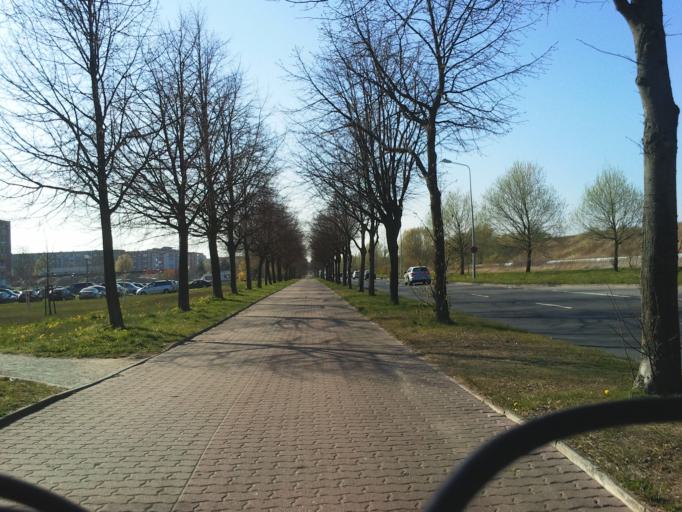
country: DE
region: Mecklenburg-Vorpommern
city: Dierkow-West
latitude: 54.1141
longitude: 12.1586
